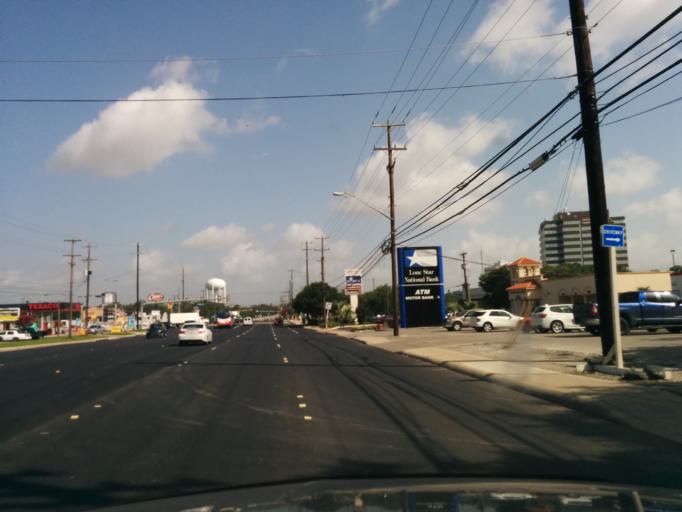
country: US
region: Texas
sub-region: Bexar County
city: Balcones Heights
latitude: 29.5117
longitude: -98.5679
